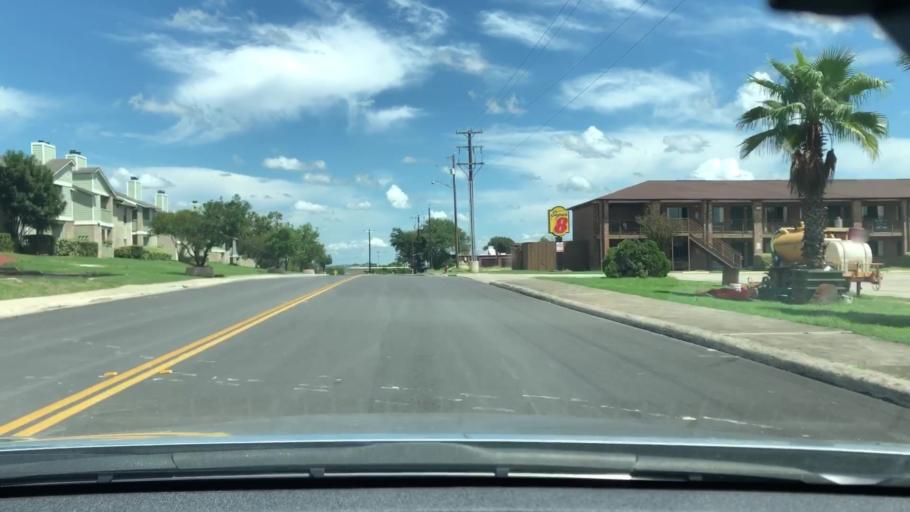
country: US
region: Texas
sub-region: Bexar County
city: Live Oak
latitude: 29.5553
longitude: -98.3208
